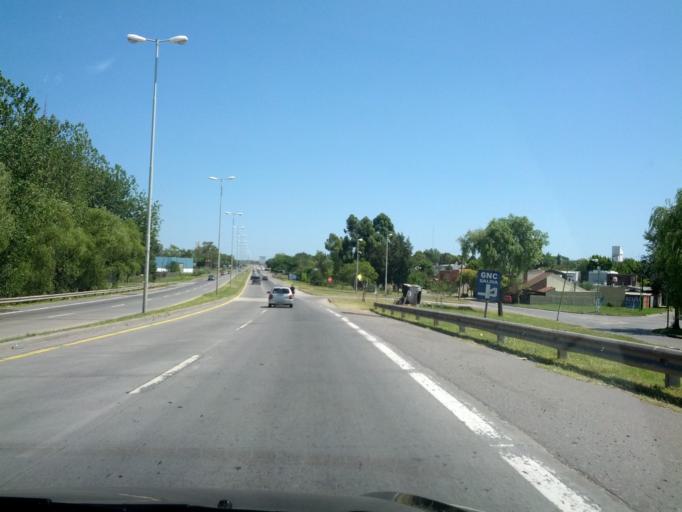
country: AR
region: Buenos Aires
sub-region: Partido de Campana
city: Campana
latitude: -34.1699
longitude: -58.9721
